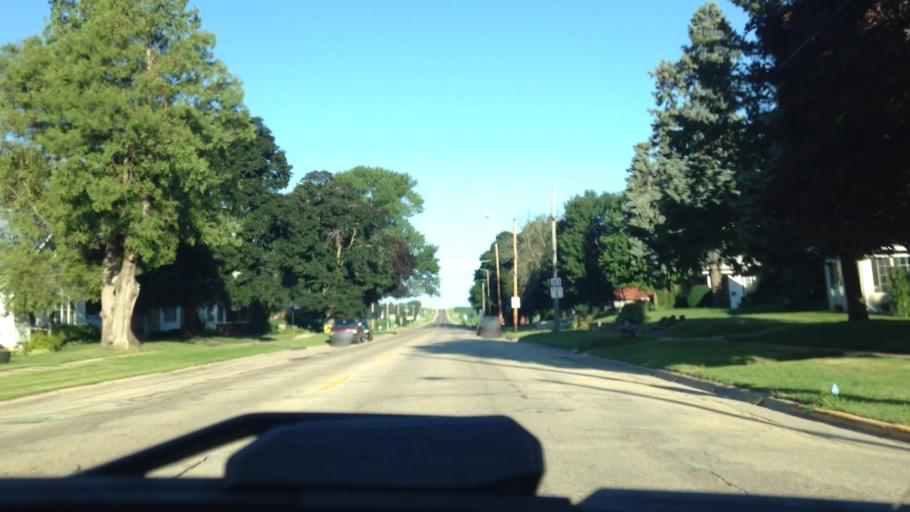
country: US
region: Wisconsin
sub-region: Columbia County
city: Poynette
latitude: 43.3376
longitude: -89.3806
